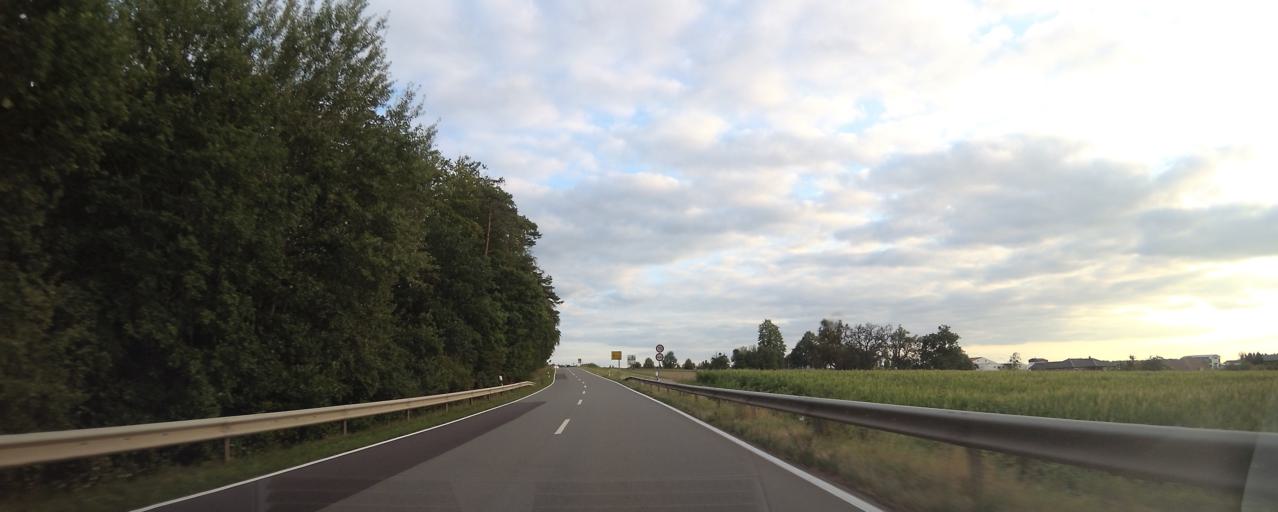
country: DE
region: Rheinland-Pfalz
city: Zemmer
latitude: 49.8998
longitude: 6.7074
